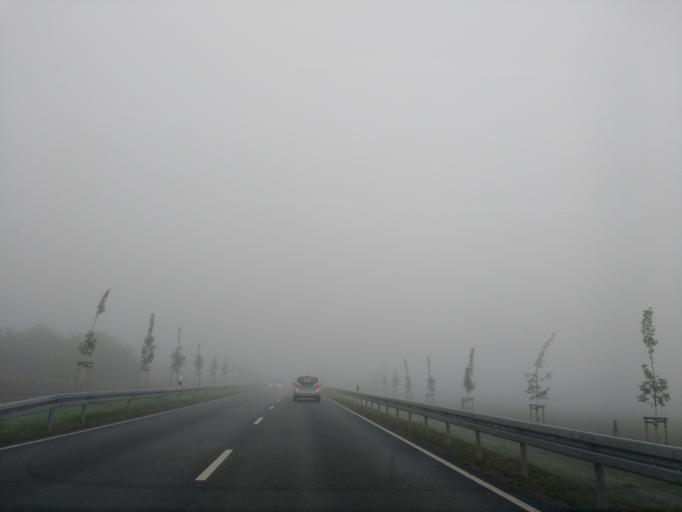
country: DE
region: Saxony-Anhalt
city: Halle (Saale)
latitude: 51.4884
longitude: 12.0174
